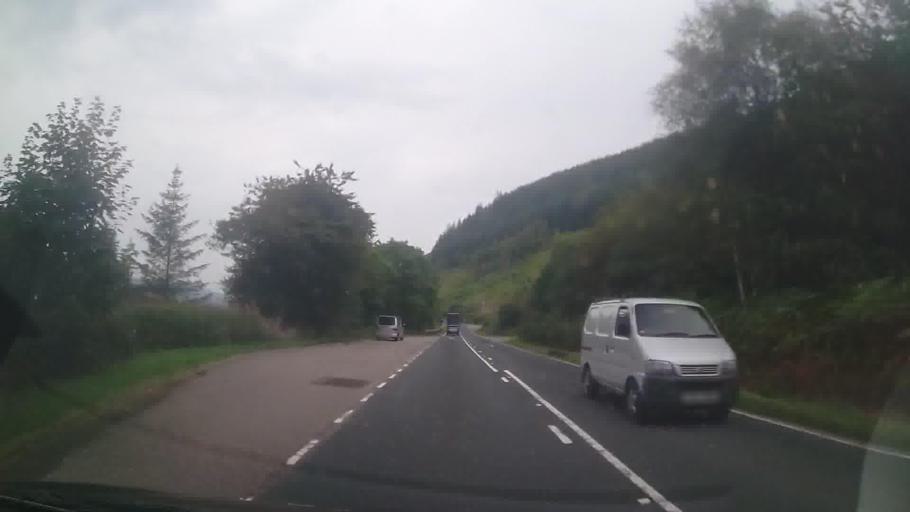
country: GB
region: Scotland
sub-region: Highland
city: Fort William
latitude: 56.7298
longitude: -5.2253
